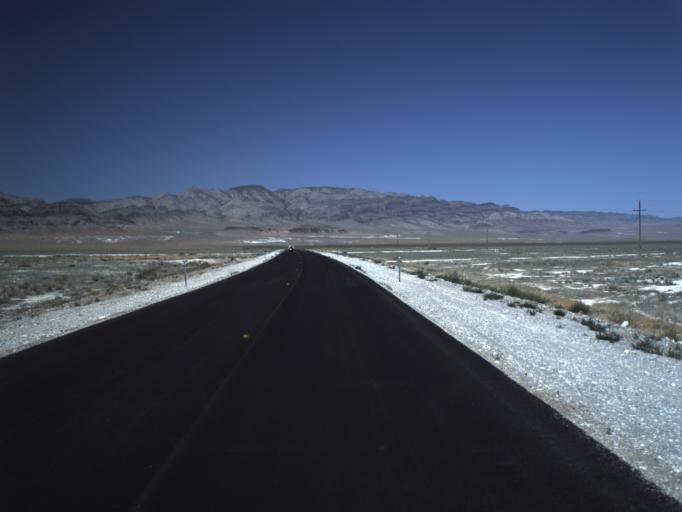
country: US
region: Utah
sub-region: Beaver County
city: Milford
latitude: 39.0644
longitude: -113.4458
